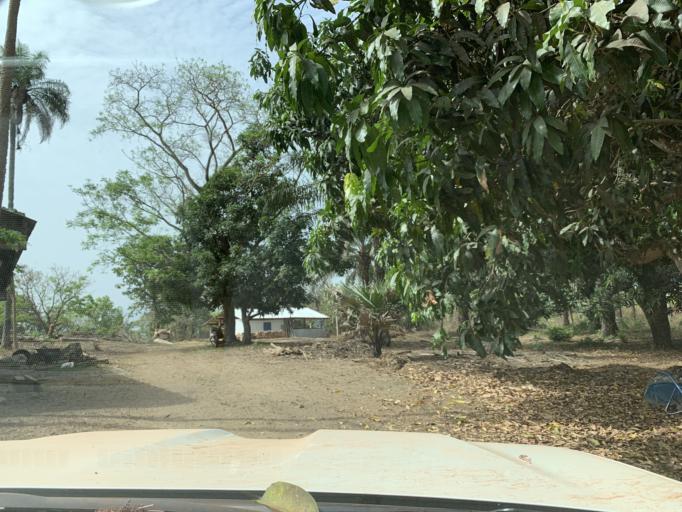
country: GN
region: Kindia
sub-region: Kindia
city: Kindia
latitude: 9.9728
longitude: -12.9849
